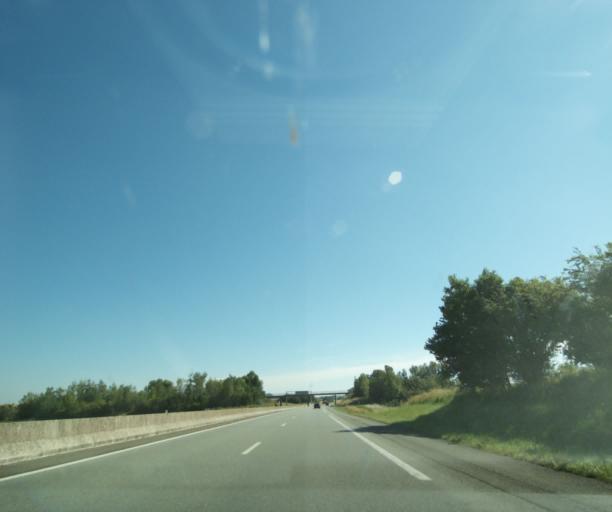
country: FR
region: Champagne-Ardenne
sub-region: Departement de la Haute-Marne
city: Avrecourt
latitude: 48.0159
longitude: 5.5246
